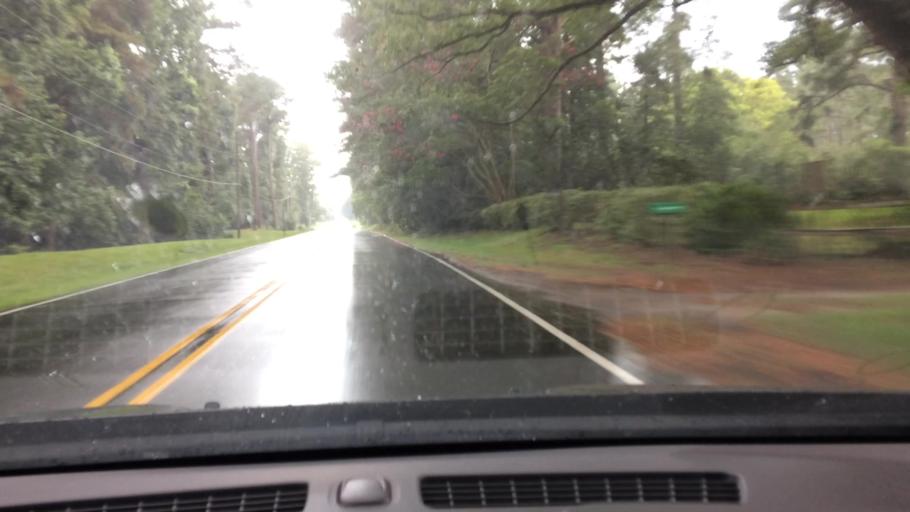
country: US
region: North Carolina
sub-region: Pitt County
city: Winterville
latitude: 35.5048
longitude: -77.3810
